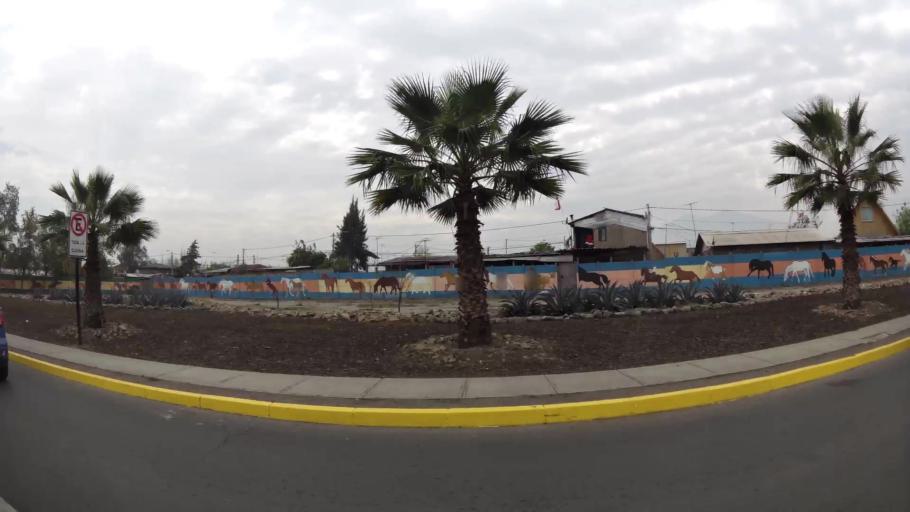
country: CL
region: Santiago Metropolitan
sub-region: Provincia de Chacabuco
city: Chicureo Abajo
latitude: -33.2049
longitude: -70.6695
